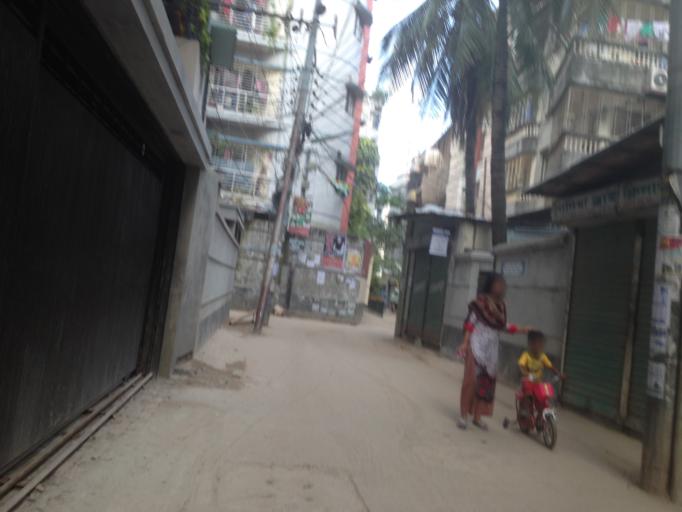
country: BD
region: Dhaka
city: Azimpur
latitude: 23.8035
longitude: 90.3718
